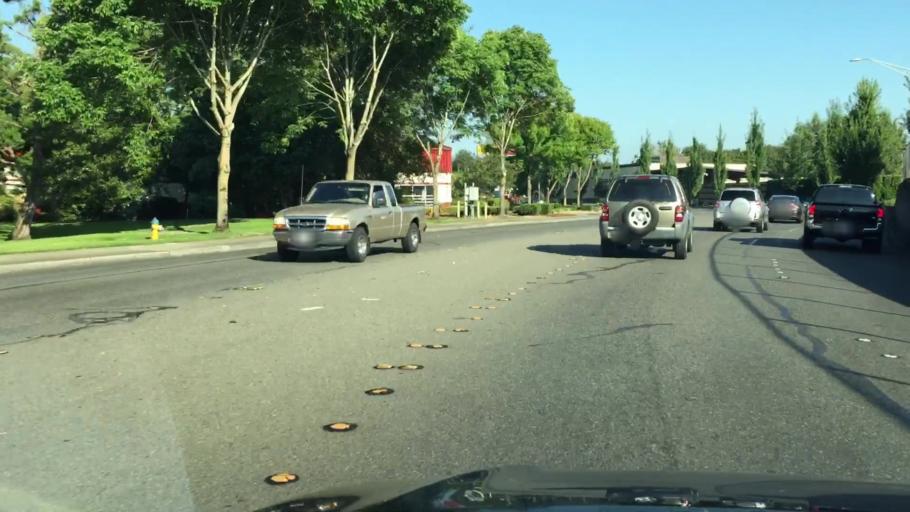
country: US
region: Washington
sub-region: King County
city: Tukwila
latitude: 47.4417
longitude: -122.2506
